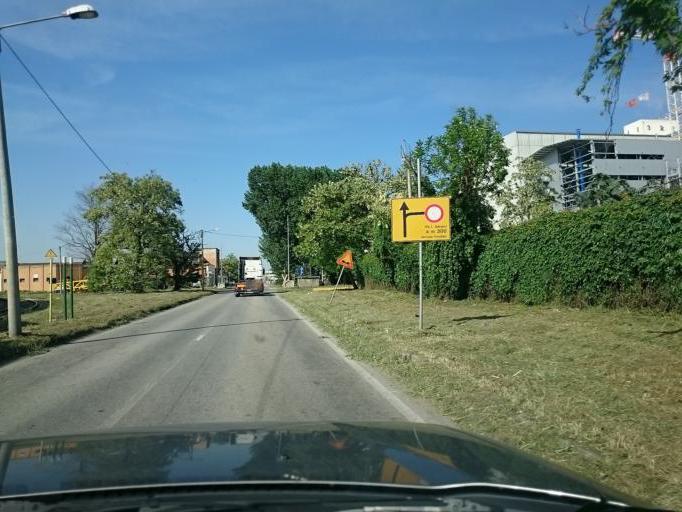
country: IT
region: Veneto
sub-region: Provincia di Venezia
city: Mestre
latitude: 45.4679
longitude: 12.2301
